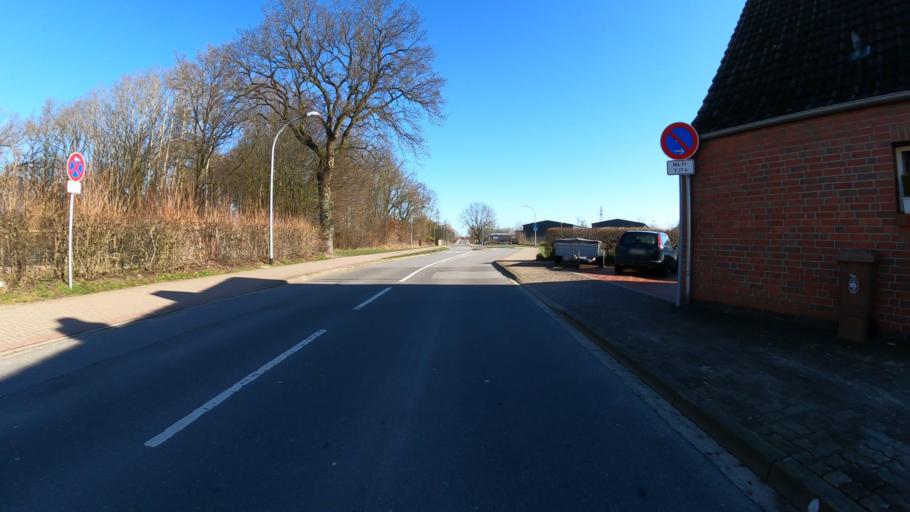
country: DE
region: Schleswig-Holstein
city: Kummerfeld
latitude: 53.6869
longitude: 9.7794
